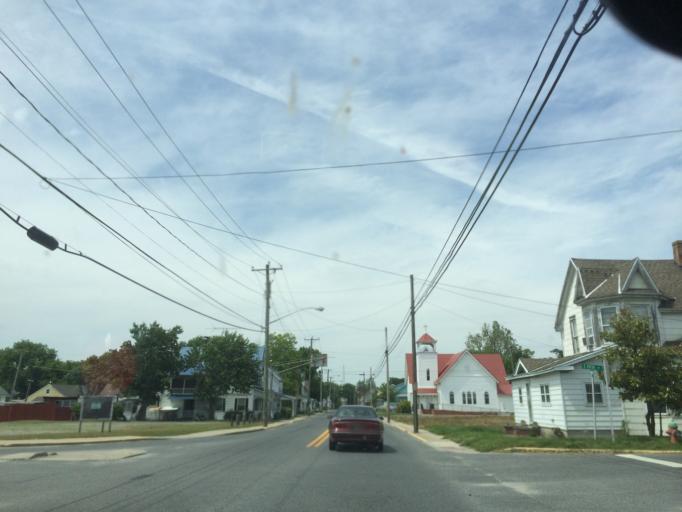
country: US
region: Delaware
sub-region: Sussex County
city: Blades
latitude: 38.6328
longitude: -75.6093
